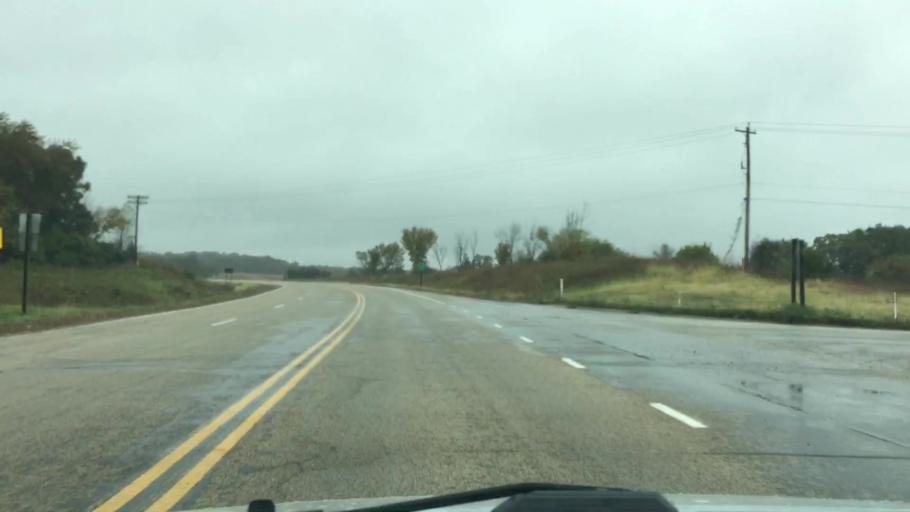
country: US
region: Wisconsin
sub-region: Jefferson County
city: Palmyra
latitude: 42.8845
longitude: -88.5603
